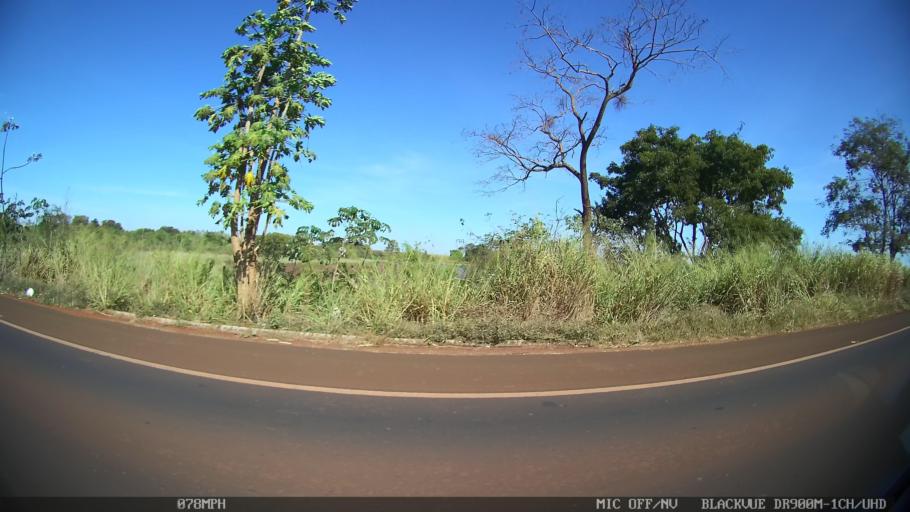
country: BR
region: Sao Paulo
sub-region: Guaira
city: Guaira
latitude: -20.4443
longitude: -48.3645
